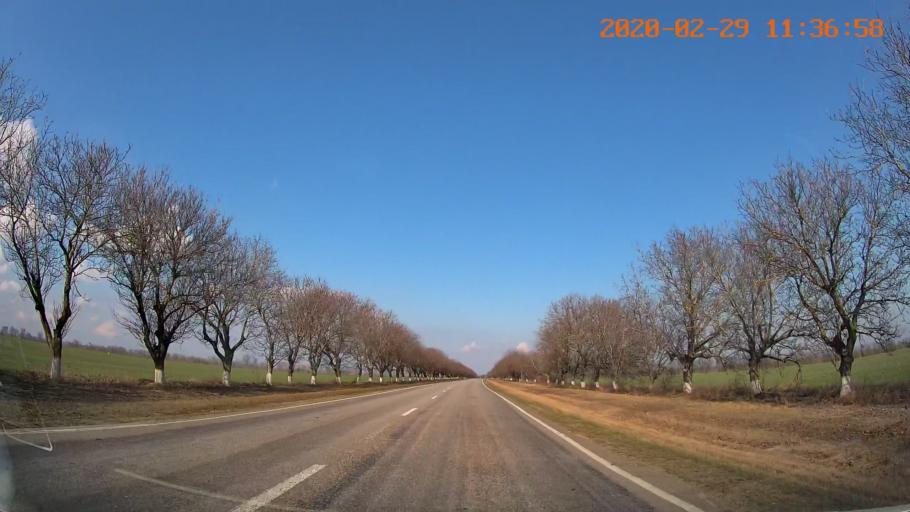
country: MD
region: Rezina
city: Saharna
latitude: 47.6044
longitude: 29.0503
